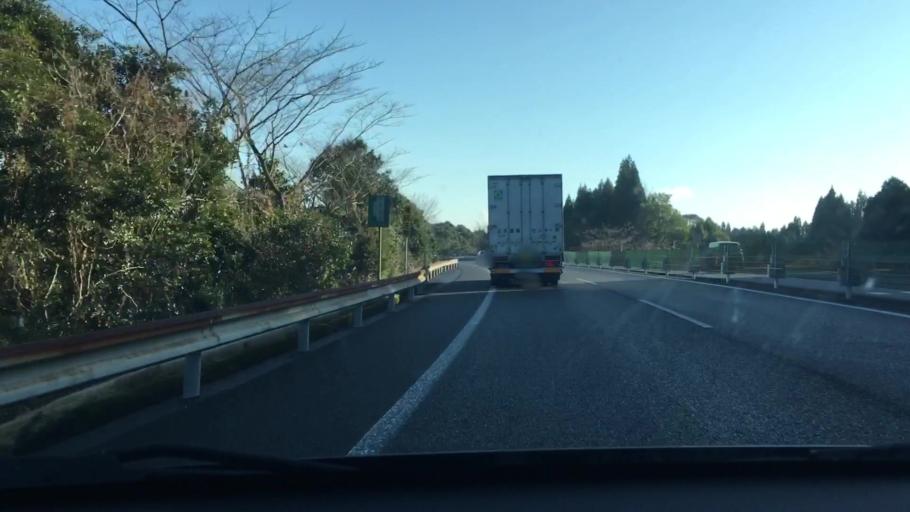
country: JP
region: Kagoshima
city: Kajiki
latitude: 31.8244
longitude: 130.6939
